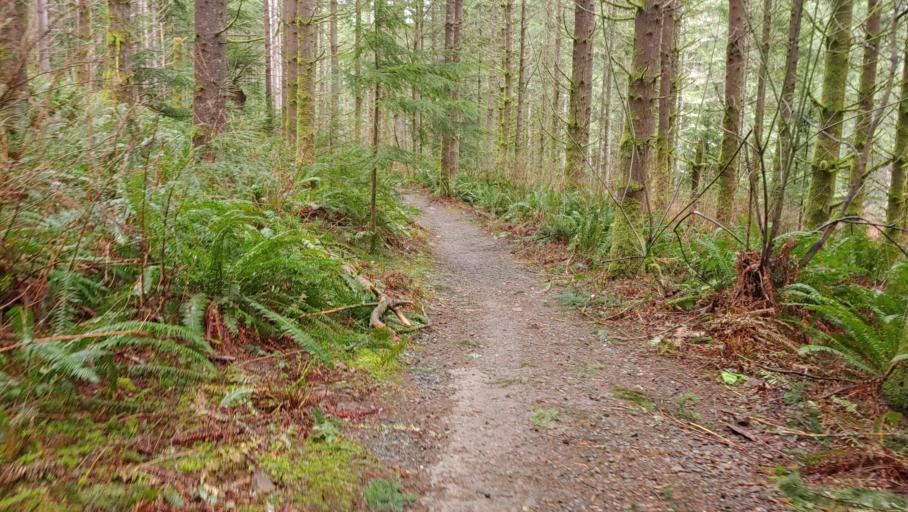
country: US
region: Washington
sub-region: King County
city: Hobart
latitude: 47.4686
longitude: -121.9333
